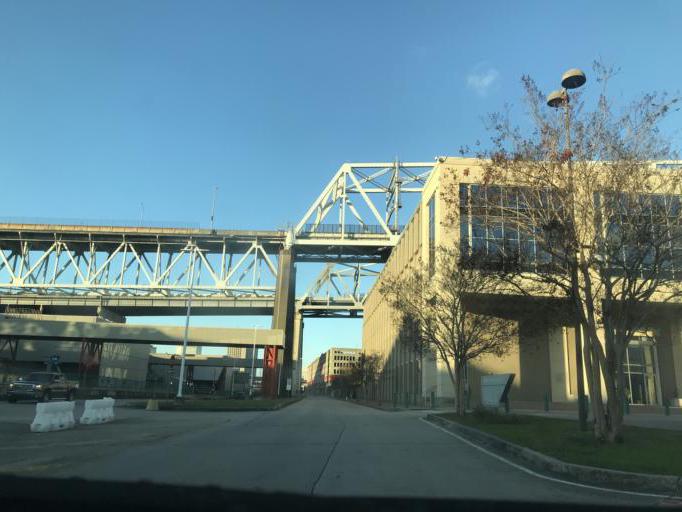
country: US
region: Louisiana
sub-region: Orleans Parish
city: New Orleans
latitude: 29.9363
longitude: -90.0617
